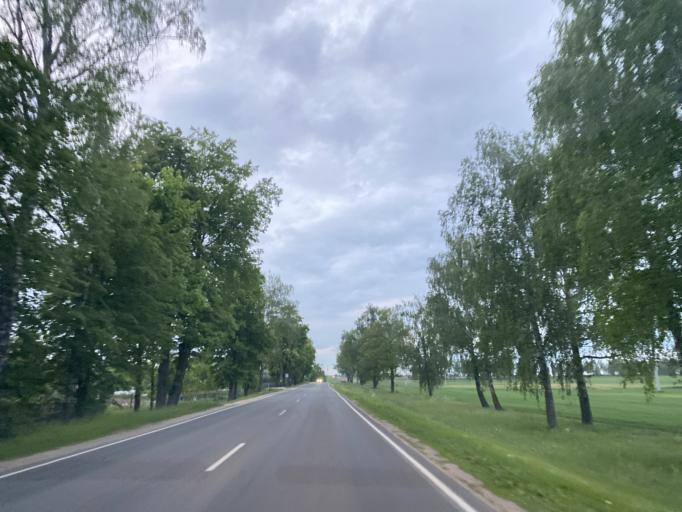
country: BY
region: Minsk
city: Rudzyensk
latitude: 53.6142
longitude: 27.8558
